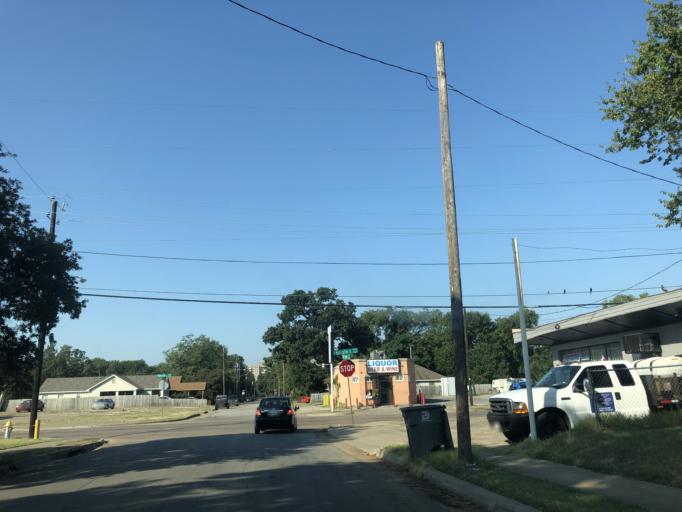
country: US
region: Texas
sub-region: Dallas County
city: Dallas
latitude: 32.7673
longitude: -96.7658
